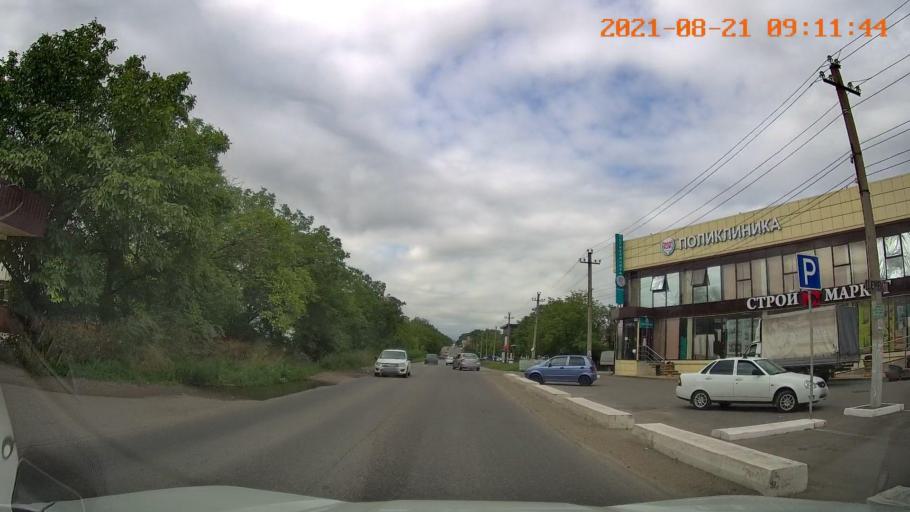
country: RU
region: Stavropol'skiy
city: Svobody
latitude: 44.0167
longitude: 43.0684
